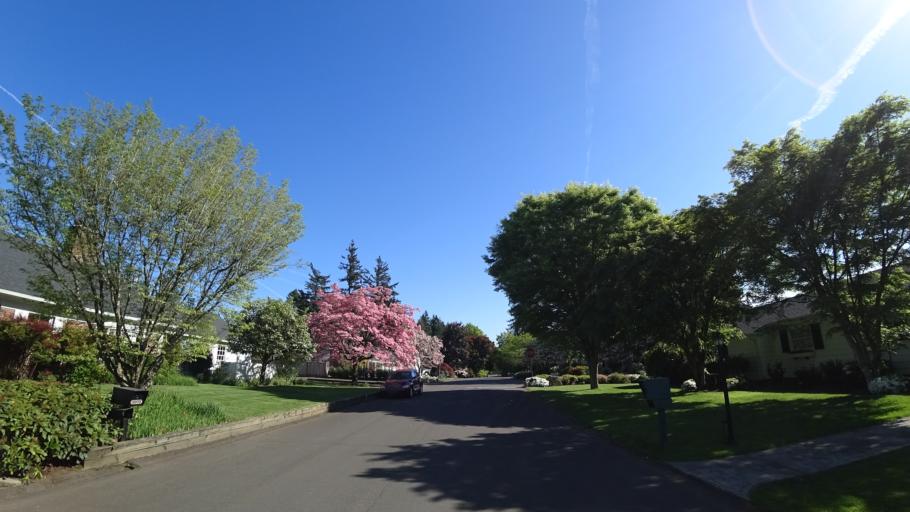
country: US
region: Oregon
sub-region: Washington County
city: West Slope
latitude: 45.4913
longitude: -122.7545
